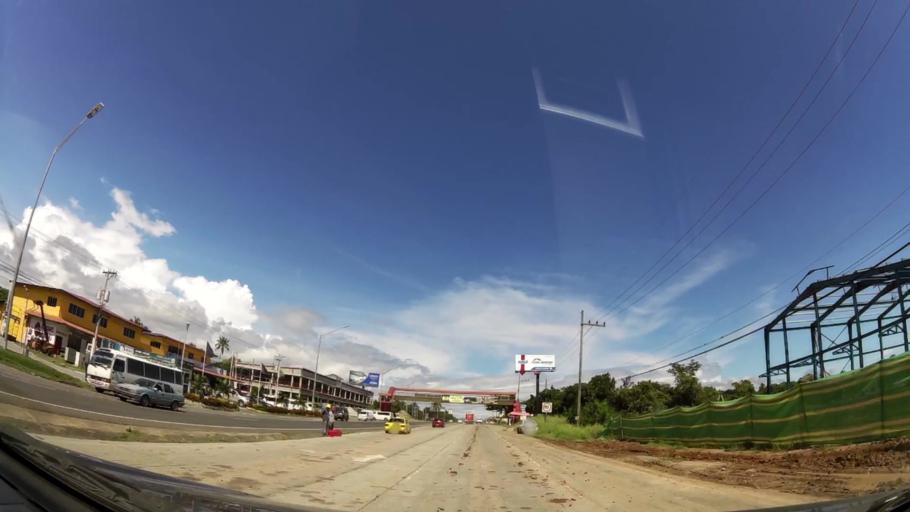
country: PA
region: Panama
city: Nueva Gorgona
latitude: 8.5458
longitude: -79.9122
